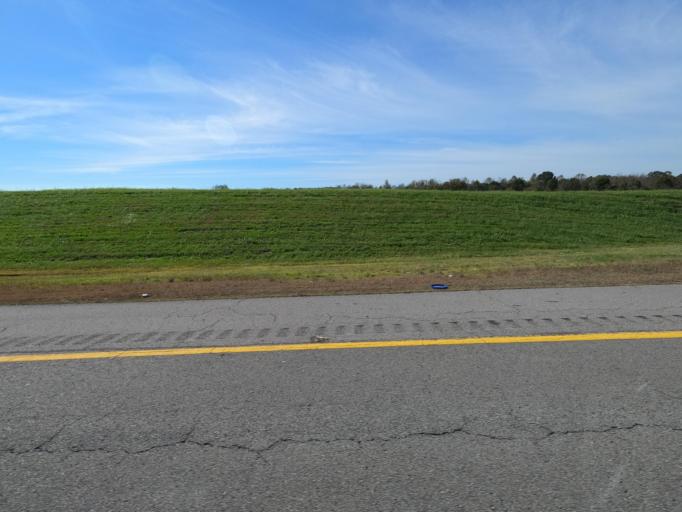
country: US
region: Tennessee
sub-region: Dickson County
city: Burns
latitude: 36.0214
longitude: -87.2629
